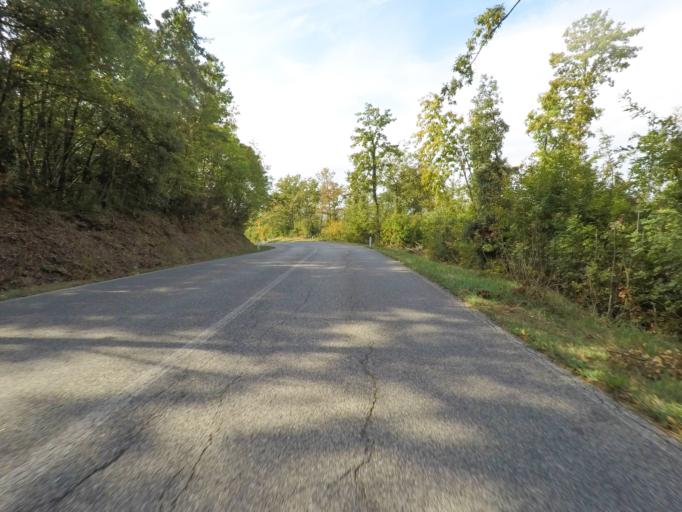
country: IT
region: Tuscany
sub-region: Provincia di Siena
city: Belverde
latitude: 43.3844
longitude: 11.3437
